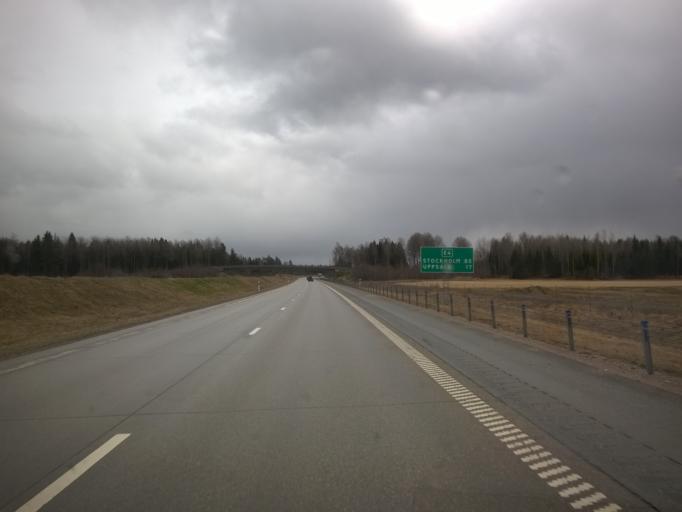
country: SE
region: Uppsala
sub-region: Uppsala Kommun
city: Storvreta
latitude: 60.0035
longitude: 17.6293
